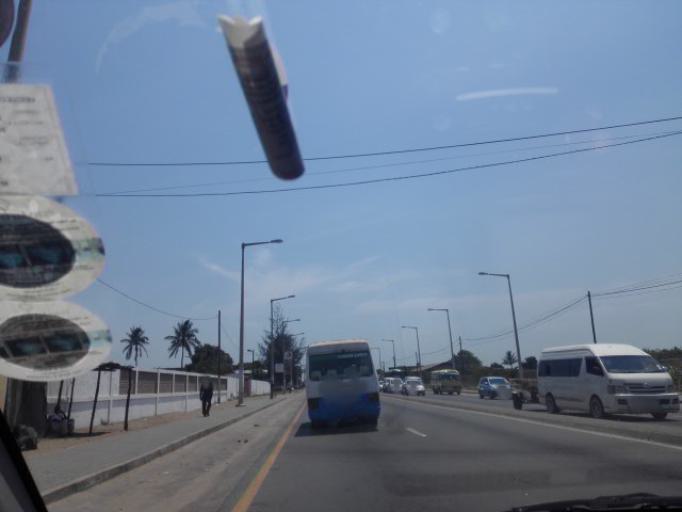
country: MZ
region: Maputo City
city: Maputo
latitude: -25.9209
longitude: 32.5629
